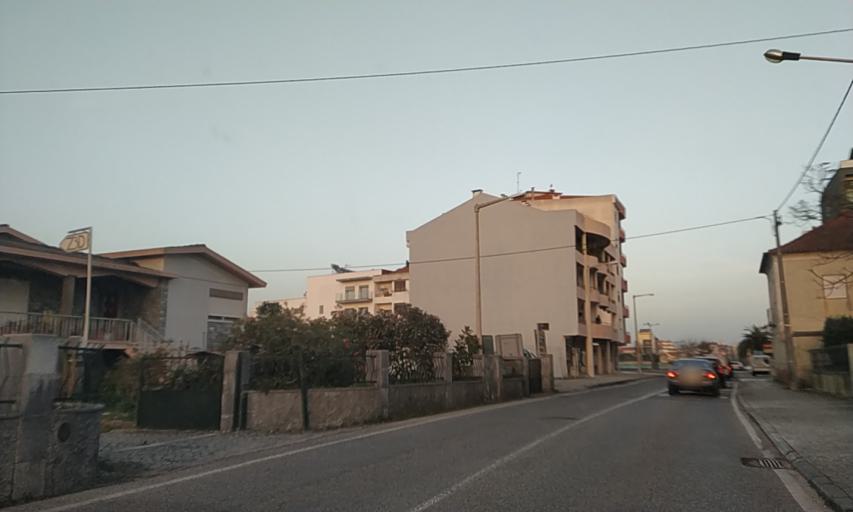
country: PT
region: Leiria
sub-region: Marinha Grande
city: Marinha Grande
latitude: 39.7472
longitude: -8.9379
